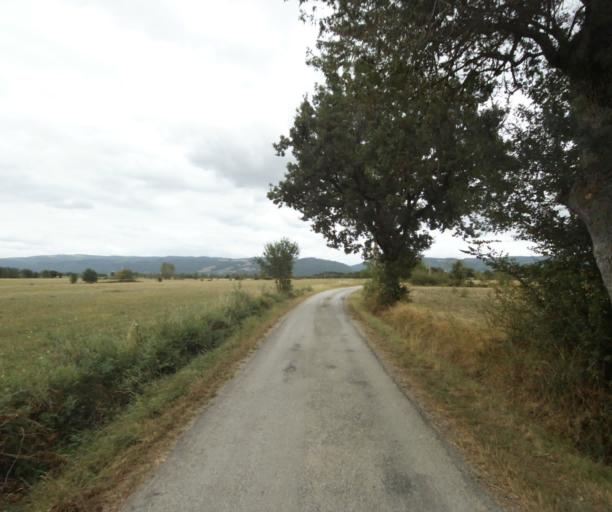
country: FR
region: Midi-Pyrenees
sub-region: Departement de la Haute-Garonne
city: Revel
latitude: 43.4790
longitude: 2.0320
